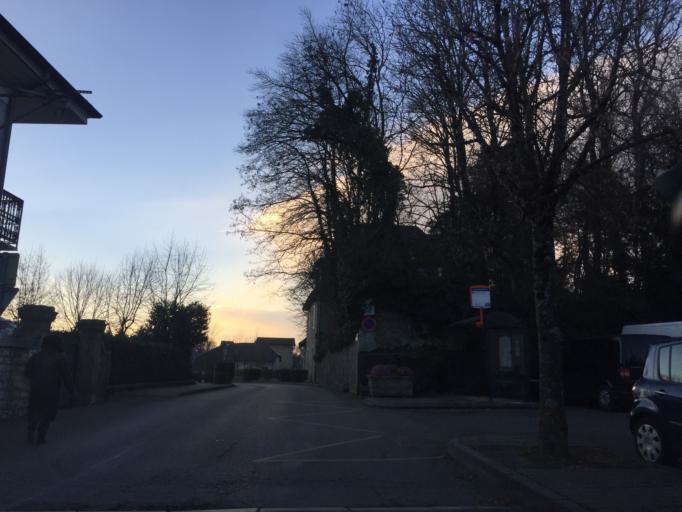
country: FR
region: Rhone-Alpes
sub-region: Departement de la Savoie
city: Tresserve
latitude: 45.6767
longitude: 5.8998
